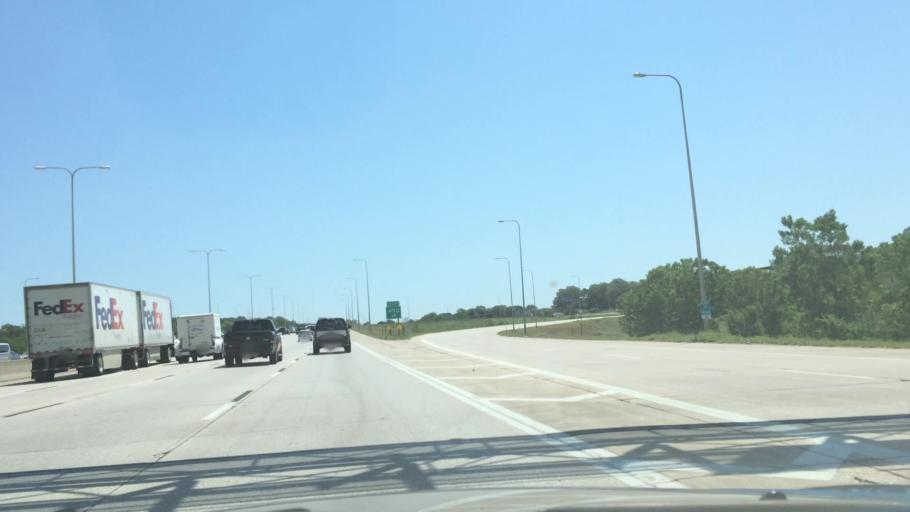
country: US
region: Nebraska
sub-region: Douglas County
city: Ralston
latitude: 41.2236
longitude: -96.0110
